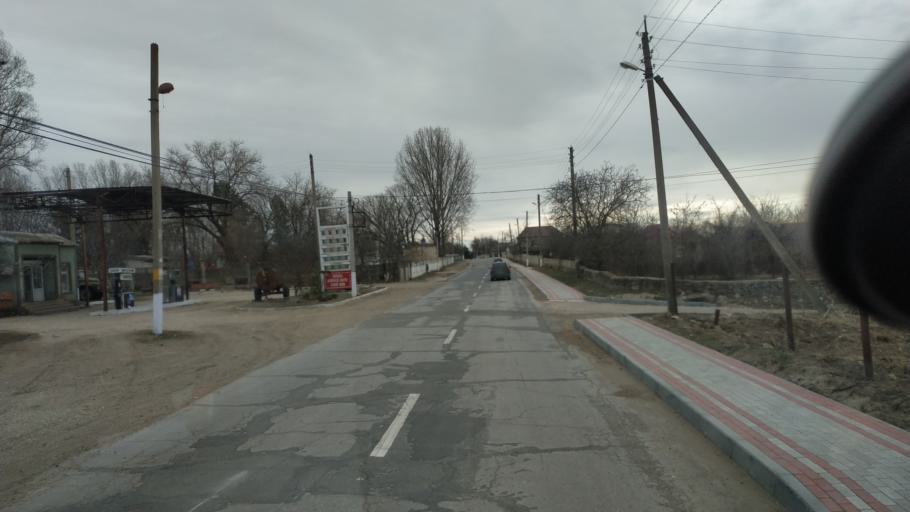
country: MD
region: Telenesti
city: Cocieri
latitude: 47.3133
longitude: 29.1057
